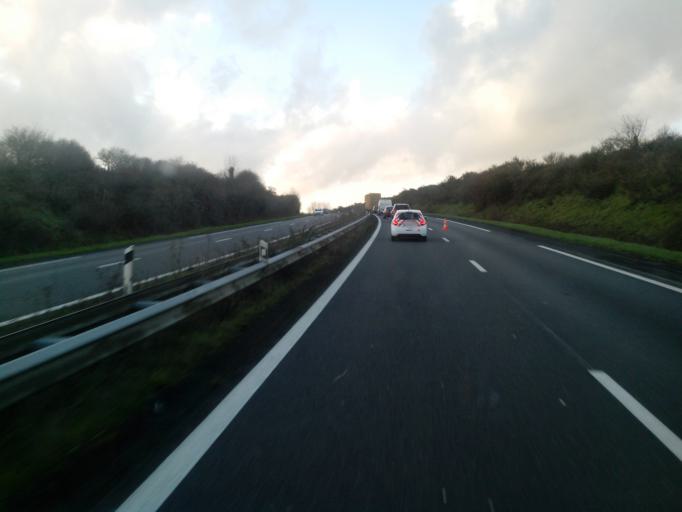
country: FR
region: Pays de la Loire
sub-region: Departement de la Loire-Atlantique
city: La Regrippiere
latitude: 47.1535
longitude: -1.2012
